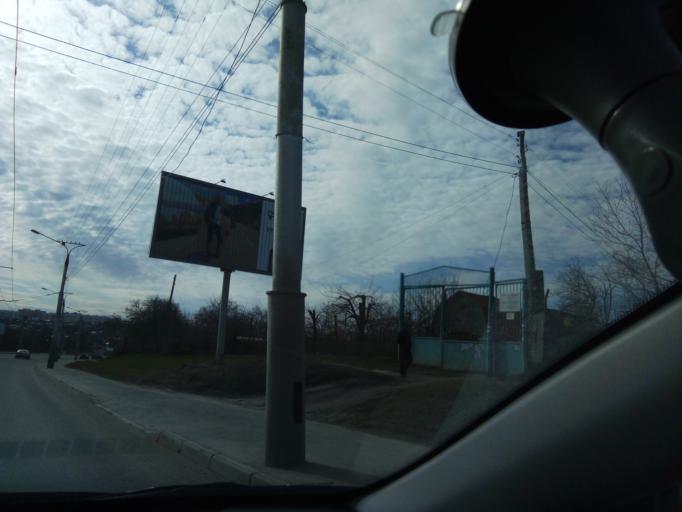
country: RU
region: Chuvashia
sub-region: Cheboksarskiy Rayon
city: Cheboksary
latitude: 56.1213
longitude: 47.2446
